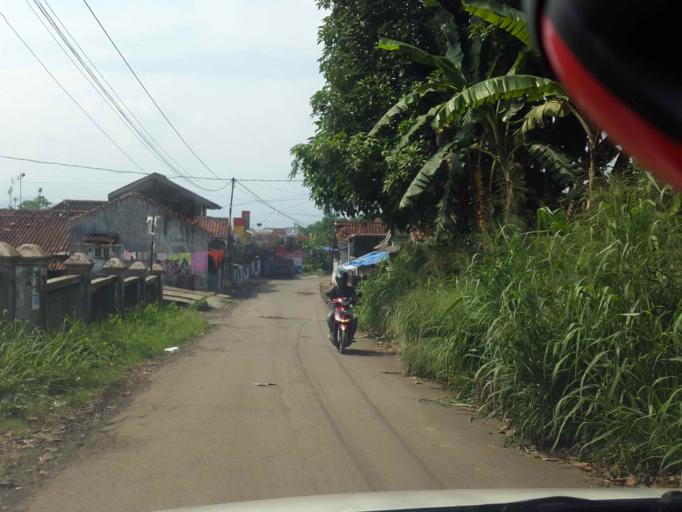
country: ID
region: West Java
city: Sukabumi
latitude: -6.9172
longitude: 106.9758
